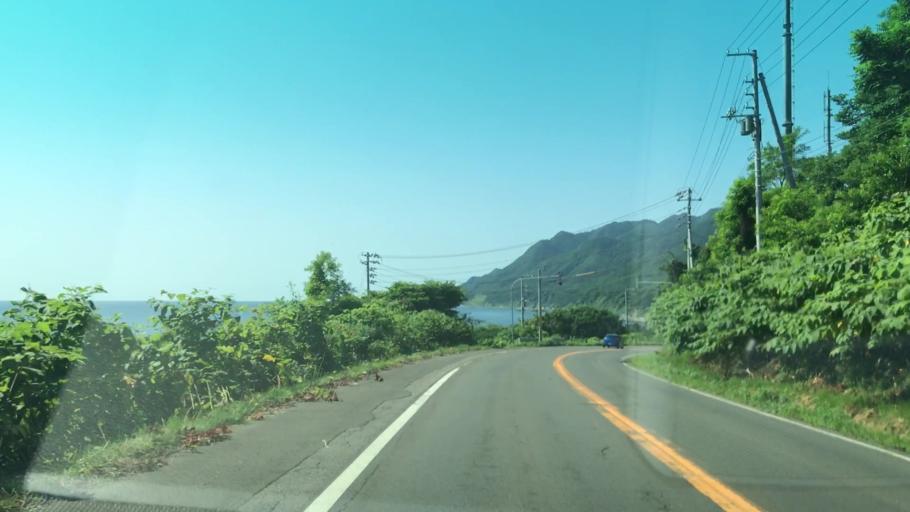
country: JP
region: Hokkaido
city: Iwanai
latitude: 43.1352
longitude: 140.4309
